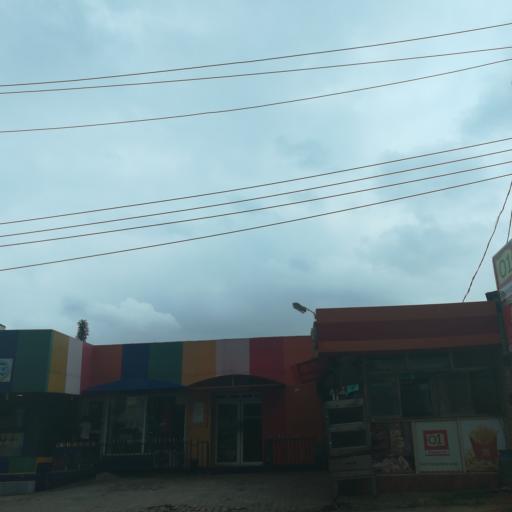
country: NG
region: Lagos
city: Ikeja
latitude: 6.6125
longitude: 3.3455
